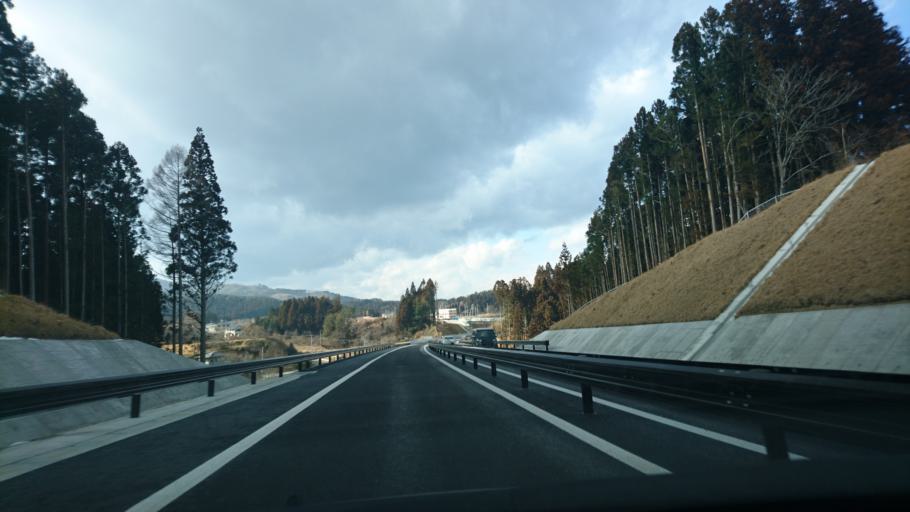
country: JP
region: Miyagi
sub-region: Oshika Gun
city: Onagawa Cho
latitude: 38.7602
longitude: 141.5017
